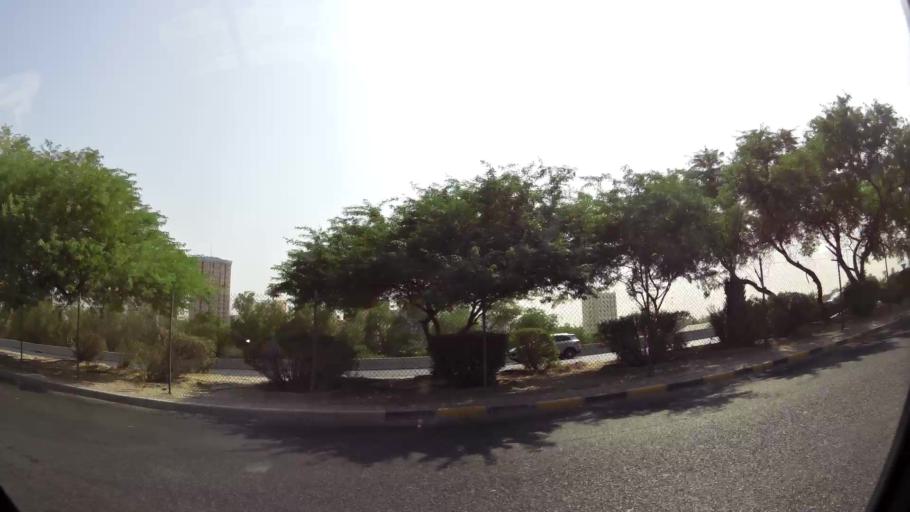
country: KW
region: Al Asimah
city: Ad Dasmah
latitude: 29.3413
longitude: 48.0019
